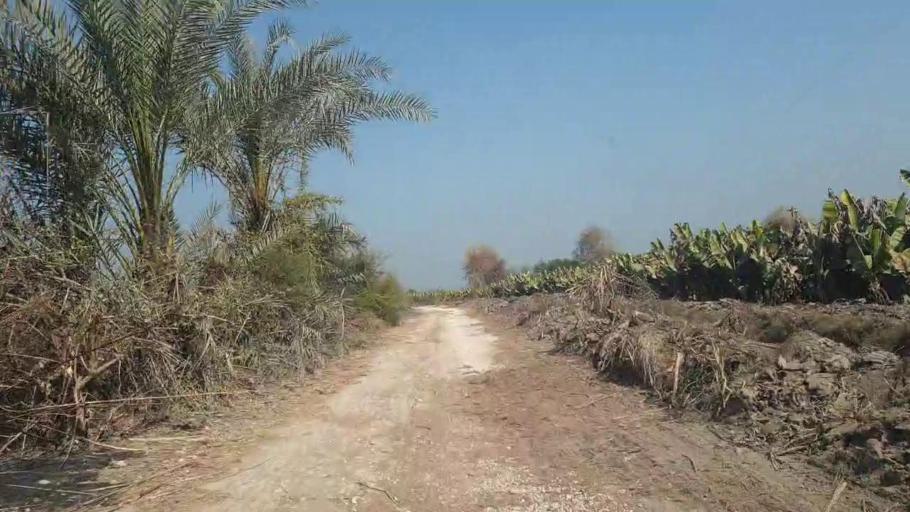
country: PK
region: Sindh
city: Sakrand
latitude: 26.0525
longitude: 68.4488
